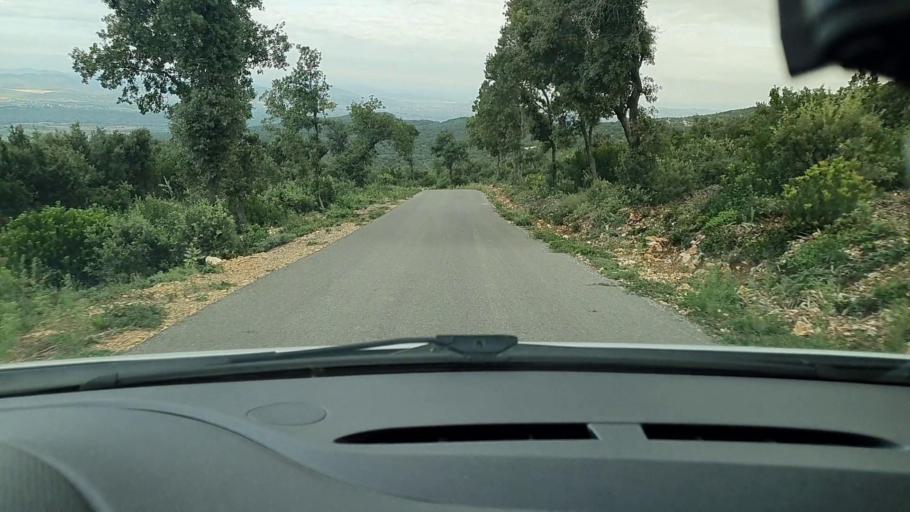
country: FR
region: Languedoc-Roussillon
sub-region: Departement du Gard
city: Mons
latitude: 44.1390
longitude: 4.2728
